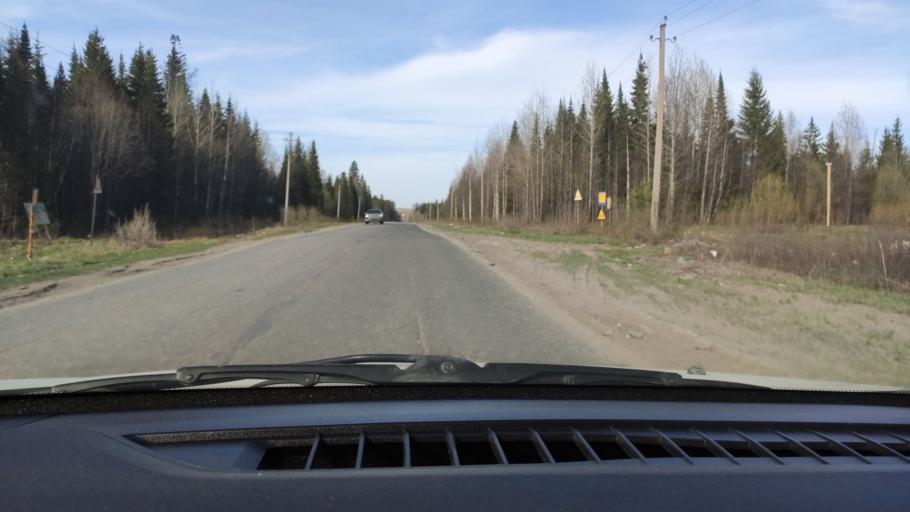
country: RU
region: Perm
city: Novyye Lyady
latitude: 57.9460
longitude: 56.5026
